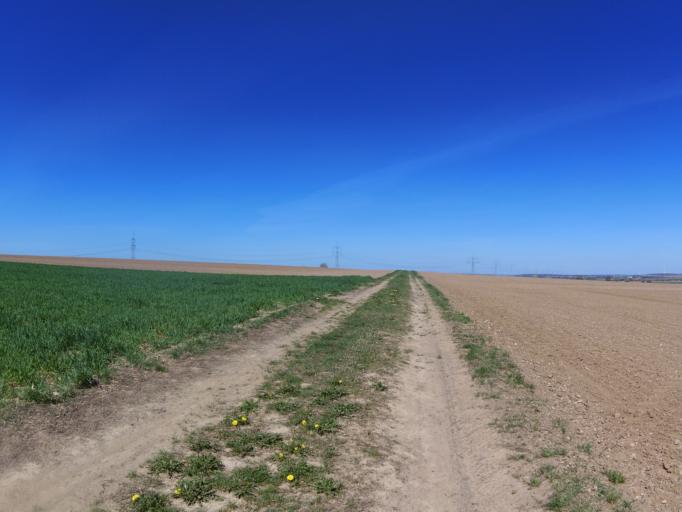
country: DE
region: Bavaria
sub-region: Regierungsbezirk Unterfranken
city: Biebelried
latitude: 49.8027
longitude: 10.0834
